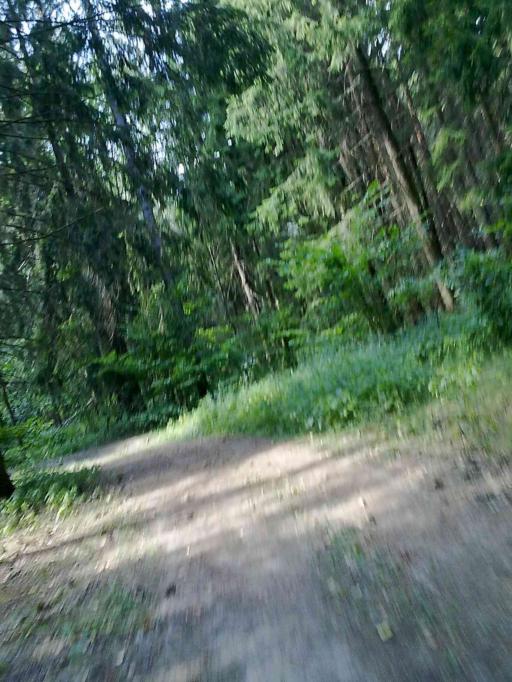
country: RU
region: Moskovskaya
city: Filimonki
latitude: 55.5536
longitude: 37.3919
